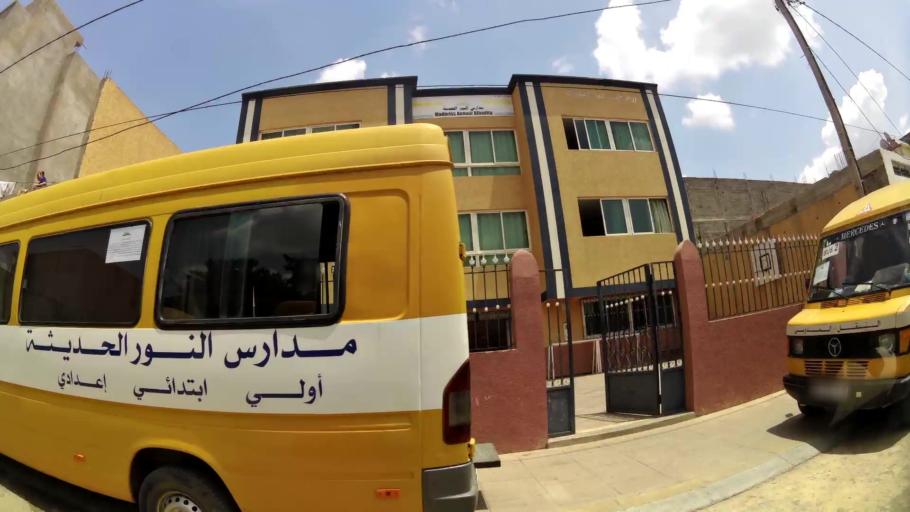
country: MA
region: Rabat-Sale-Zemmour-Zaer
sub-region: Khemisset
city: Tiflet
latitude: 34.0011
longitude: -6.5319
